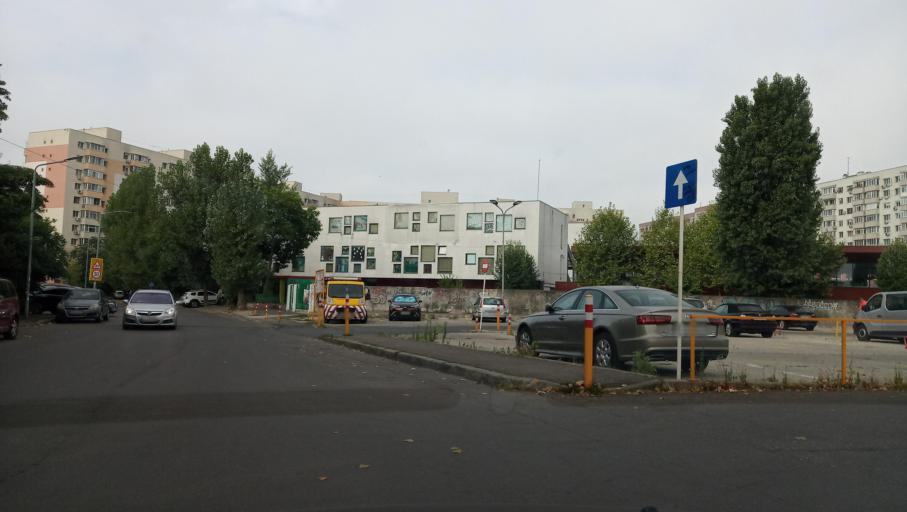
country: RO
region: Ilfov
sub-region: Comuna Popesti-Leordeni
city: Popesti-Leordeni
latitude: 44.4180
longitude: 26.1605
